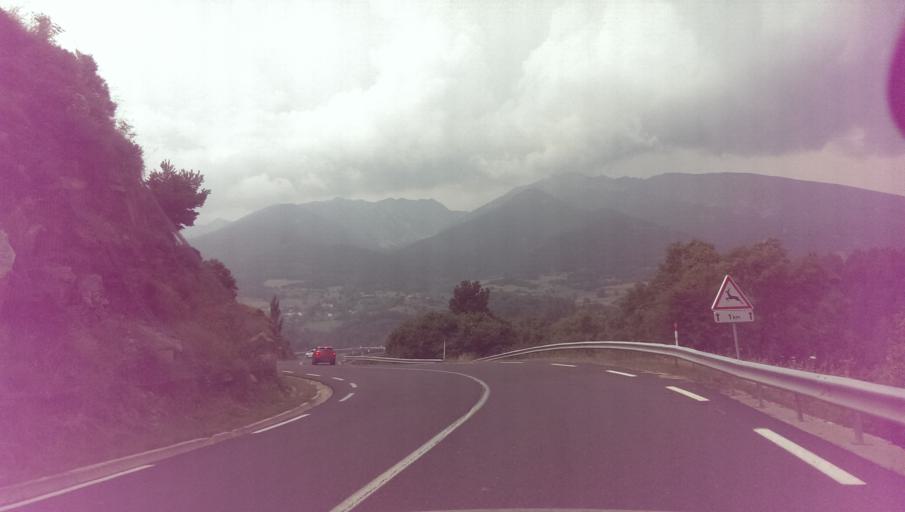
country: ES
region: Catalonia
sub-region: Provincia de Girona
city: Llivia
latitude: 42.5083
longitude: 2.1303
